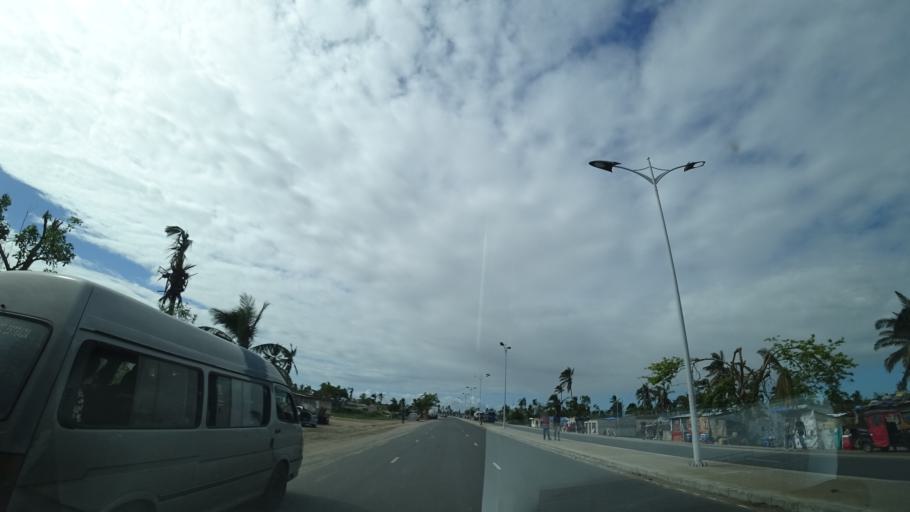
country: MZ
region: Sofala
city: Beira
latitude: -19.7801
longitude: 34.8802
